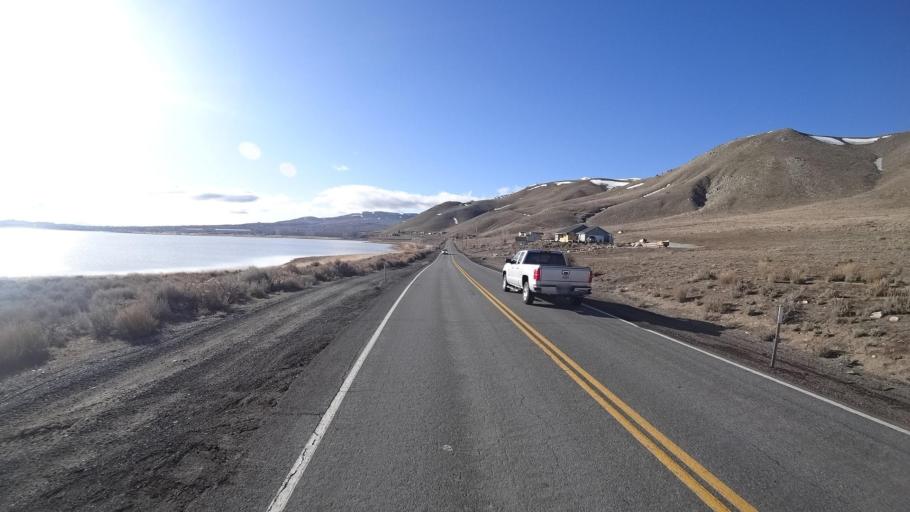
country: US
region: Nevada
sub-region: Washoe County
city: Cold Springs
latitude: 39.6461
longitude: -119.9266
